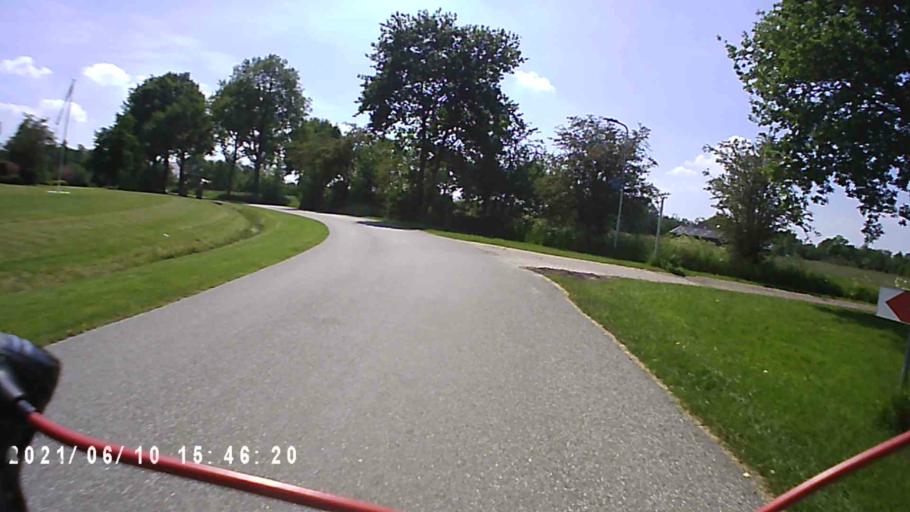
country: NL
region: Friesland
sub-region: Gemeente Achtkarspelen
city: Boelenslaan
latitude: 53.1618
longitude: 6.1221
